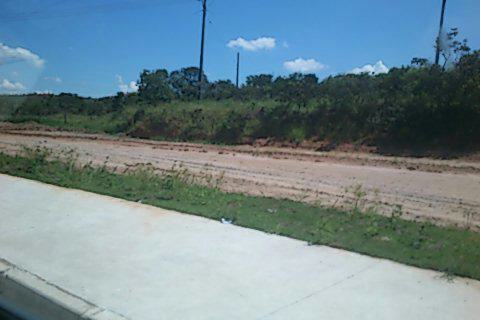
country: BR
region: Sao Paulo
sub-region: Sao Jose Dos Campos
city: Sao Jose dos Campos
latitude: -23.2437
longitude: -45.8453
